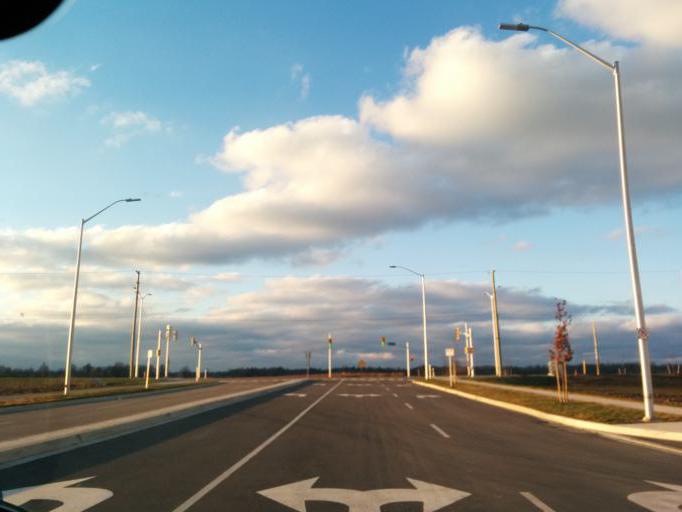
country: CA
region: Ontario
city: Oakville
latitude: 43.4496
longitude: -79.7676
